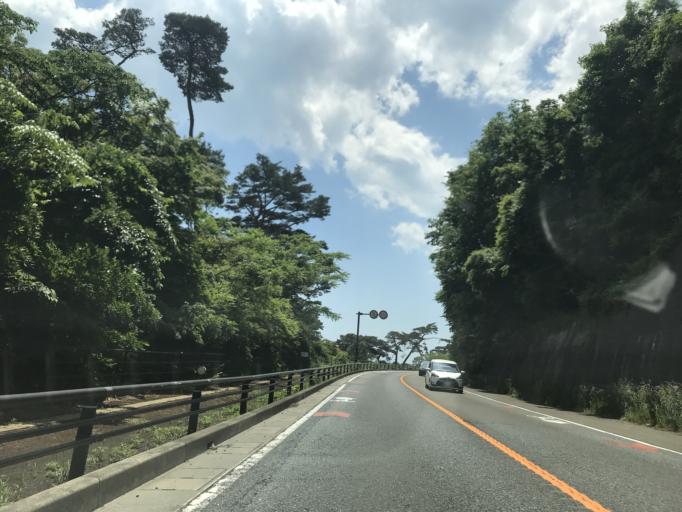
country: JP
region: Miyagi
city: Matsushima
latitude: 38.3597
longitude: 141.0622
